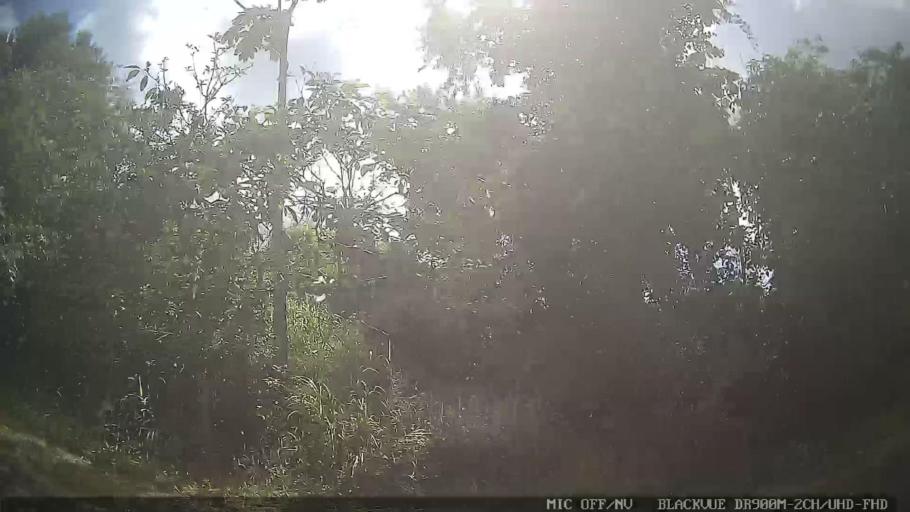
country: BR
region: Sao Paulo
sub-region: Braganca Paulista
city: Braganca Paulista
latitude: -22.8717
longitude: -46.5342
